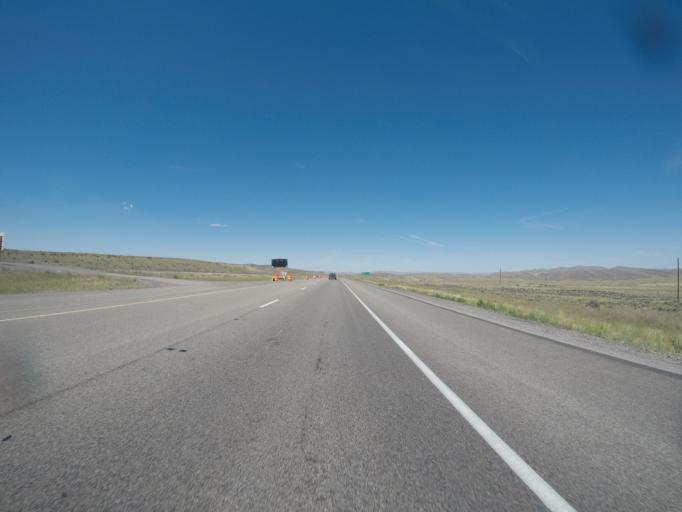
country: US
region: Wyoming
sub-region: Carbon County
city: Saratoga
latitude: 41.7423
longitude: -106.8492
